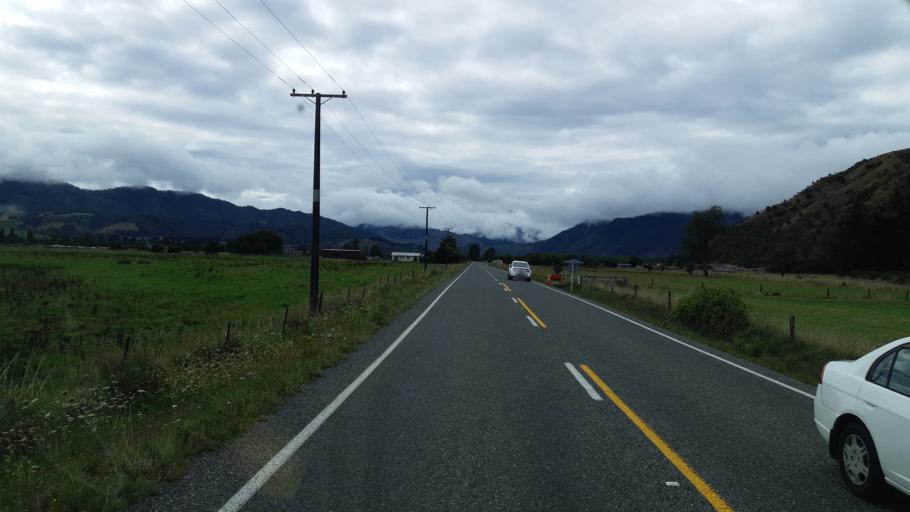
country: NZ
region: West Coast
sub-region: Buller District
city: Westport
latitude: -41.7950
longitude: 172.2963
